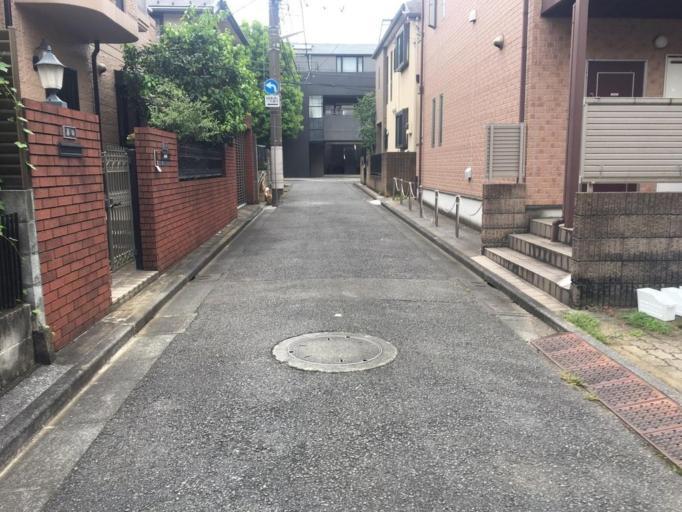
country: JP
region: Tokyo
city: Tokyo
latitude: 35.7200
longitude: 139.7004
